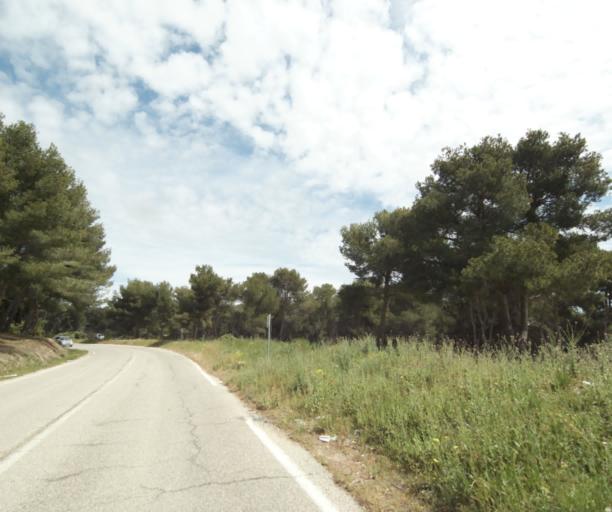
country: FR
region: Provence-Alpes-Cote d'Azur
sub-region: Departement des Bouches-du-Rhone
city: Rognac
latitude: 43.5031
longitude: 5.2084
